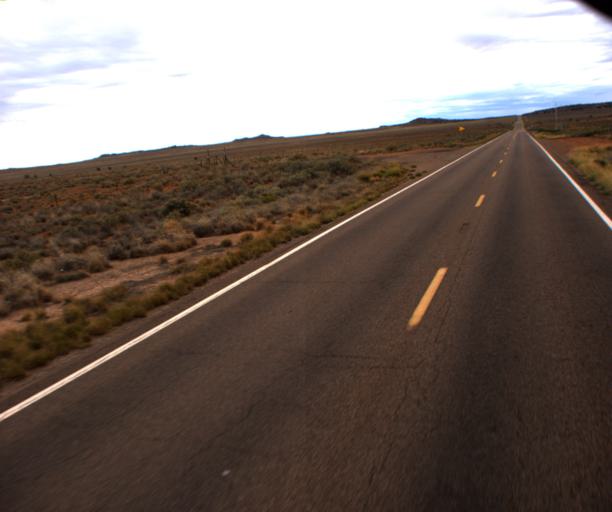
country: US
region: Arizona
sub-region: Navajo County
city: Holbrook
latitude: 34.7211
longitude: -110.1142
